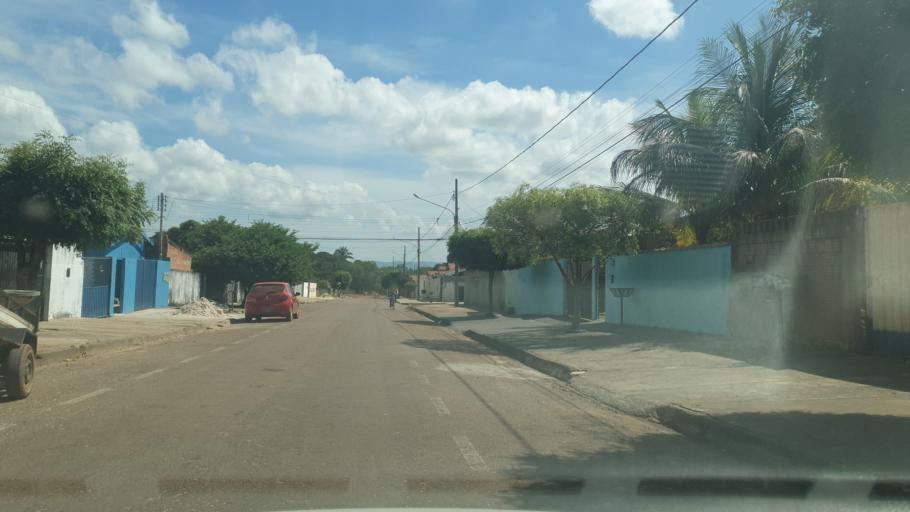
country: BR
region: Mato Grosso
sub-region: Pontes E Lacerda
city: Pontes e Lacerda
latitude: -15.2271
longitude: -59.3423
